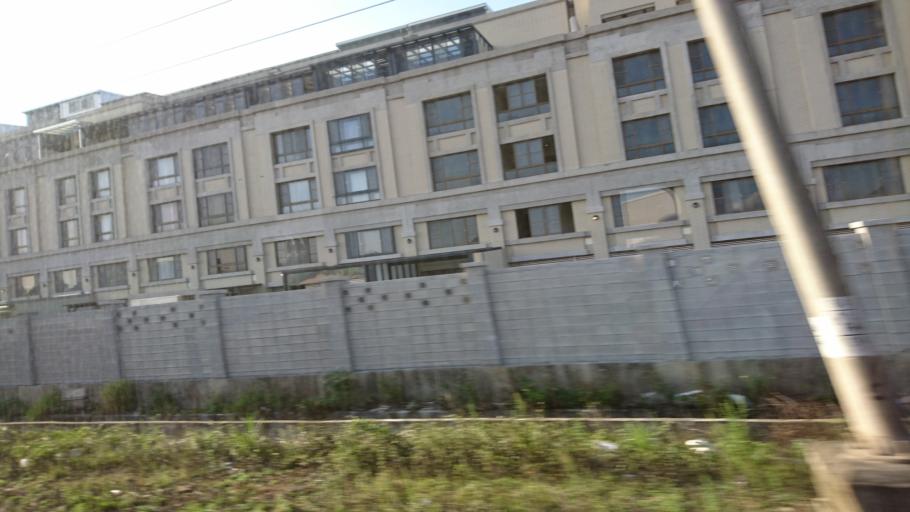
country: TW
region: Taiwan
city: Taoyuan City
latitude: 24.9653
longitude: 121.2470
